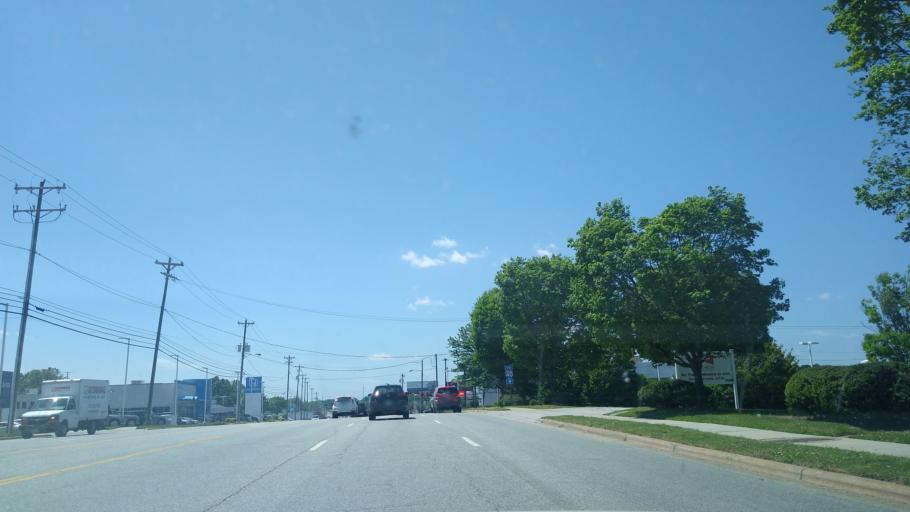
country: US
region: North Carolina
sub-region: Guilford County
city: Greensboro
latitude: 36.0604
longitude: -79.8675
